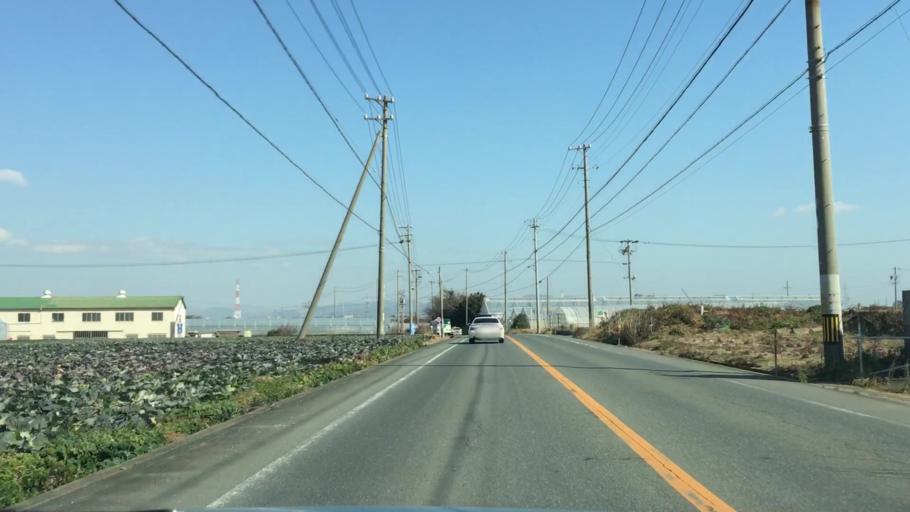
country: JP
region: Aichi
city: Toyohashi
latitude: 34.6984
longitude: 137.3425
